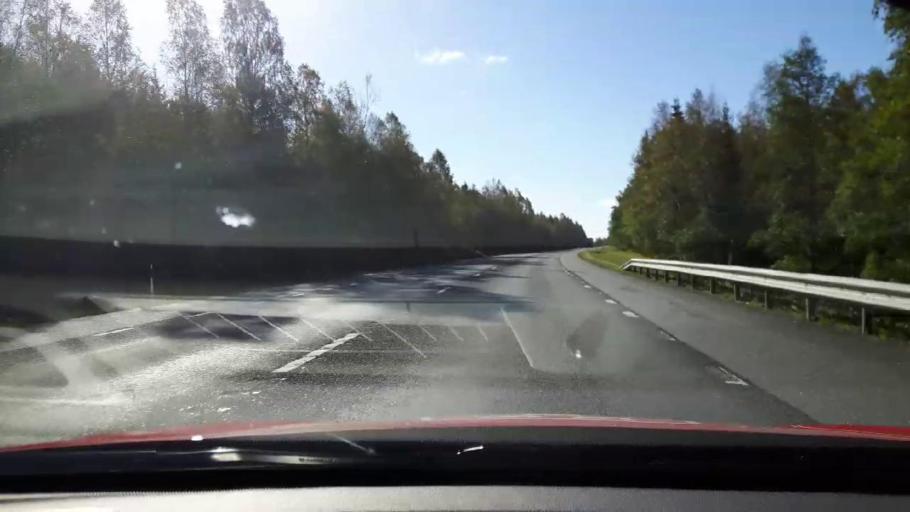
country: SE
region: Vaesternorrland
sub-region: Ange Kommun
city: Ange
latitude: 62.6535
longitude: 15.6228
